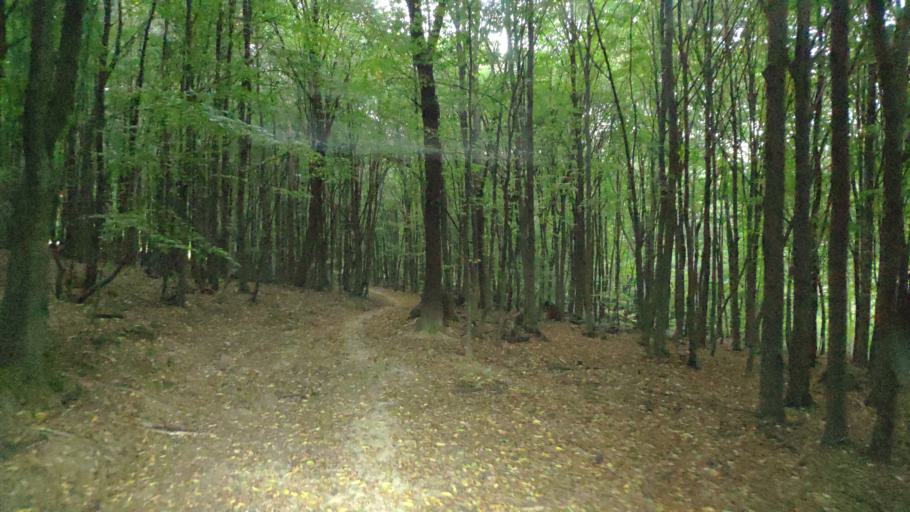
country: SK
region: Kosicky
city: Kosice
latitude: 48.7020
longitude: 21.1950
